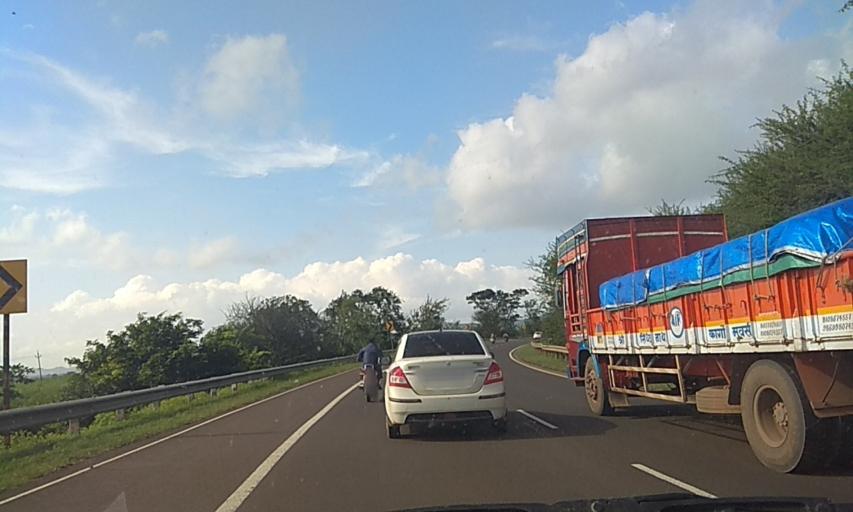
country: IN
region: Maharashtra
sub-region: Kolhapur
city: Kodoli
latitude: 16.9039
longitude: 74.2851
